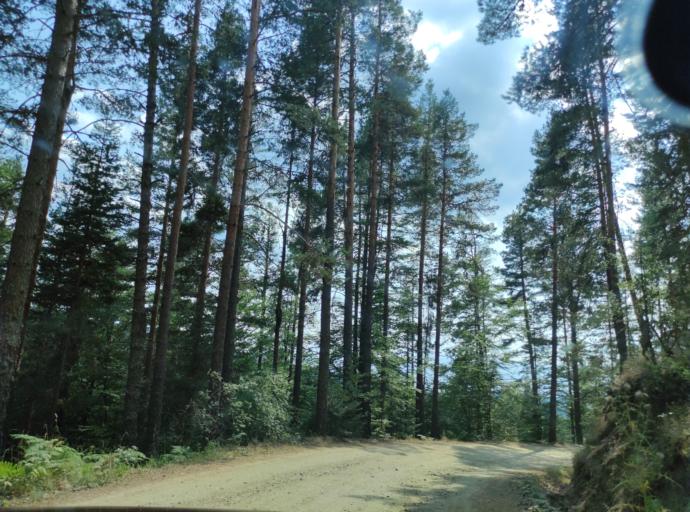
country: BG
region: Blagoevgrad
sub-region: Obshtina Belitsa
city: Belitsa
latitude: 42.0246
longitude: 23.5824
